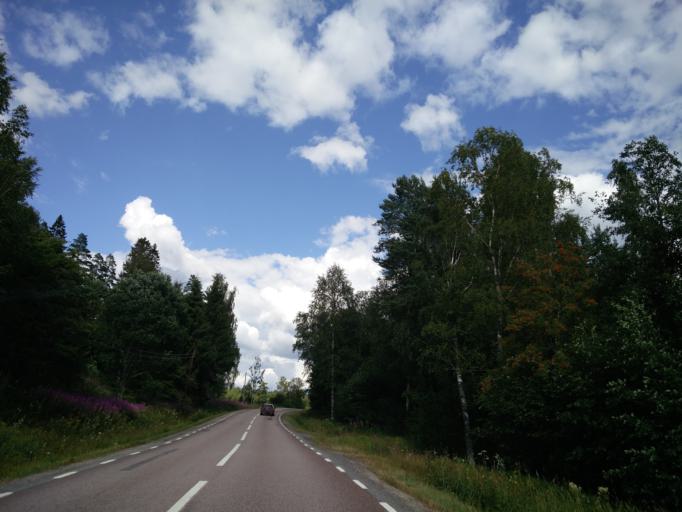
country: SE
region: Vaermland
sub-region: Sunne Kommun
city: Sunne
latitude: 59.6684
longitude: 12.9845
